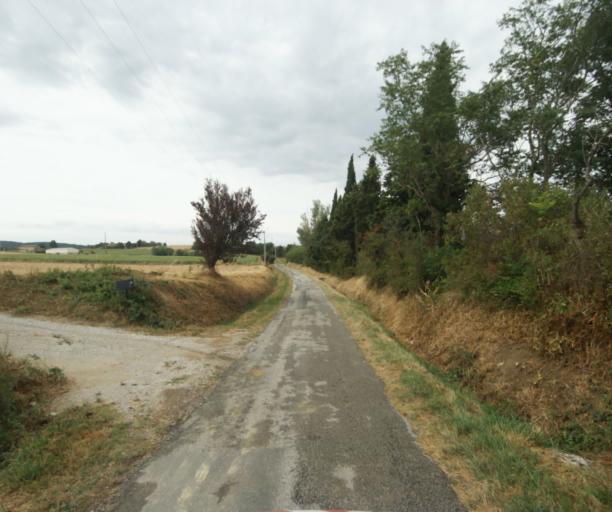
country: FR
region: Midi-Pyrenees
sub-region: Departement de la Haute-Garonne
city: Revel
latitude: 43.4349
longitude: 1.9688
